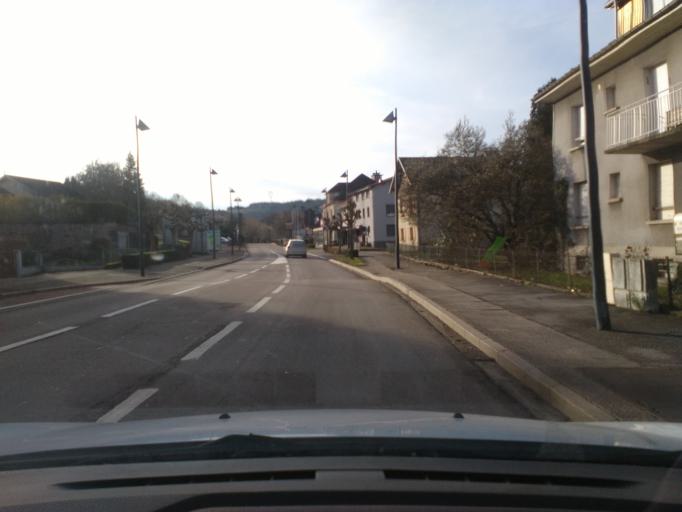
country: FR
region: Lorraine
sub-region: Departement des Vosges
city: Anould
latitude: 48.1861
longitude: 6.9473
